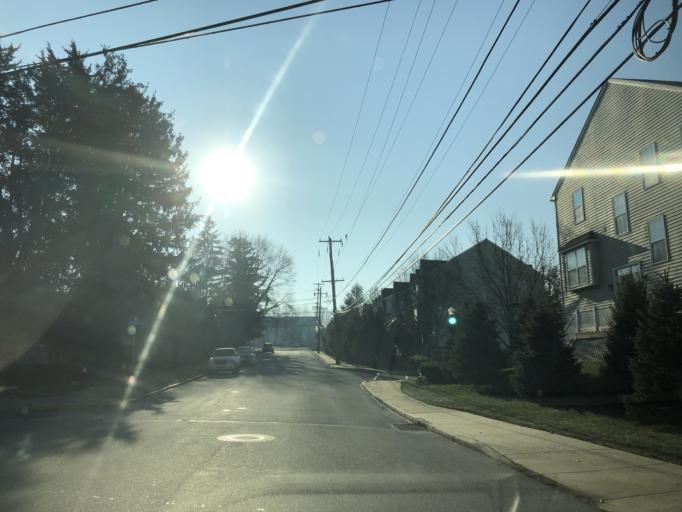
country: US
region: Pennsylvania
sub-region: Chester County
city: Downingtown
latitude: 40.0052
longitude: -75.6981
